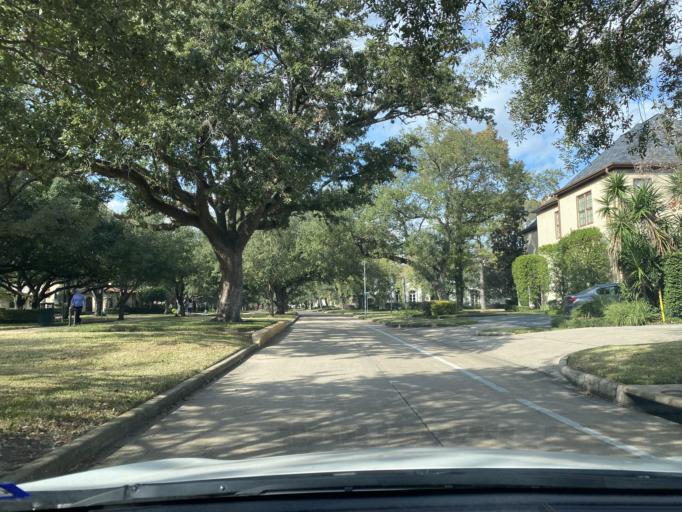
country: US
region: Texas
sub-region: Harris County
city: Hunters Creek Village
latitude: 29.7560
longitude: -95.4713
